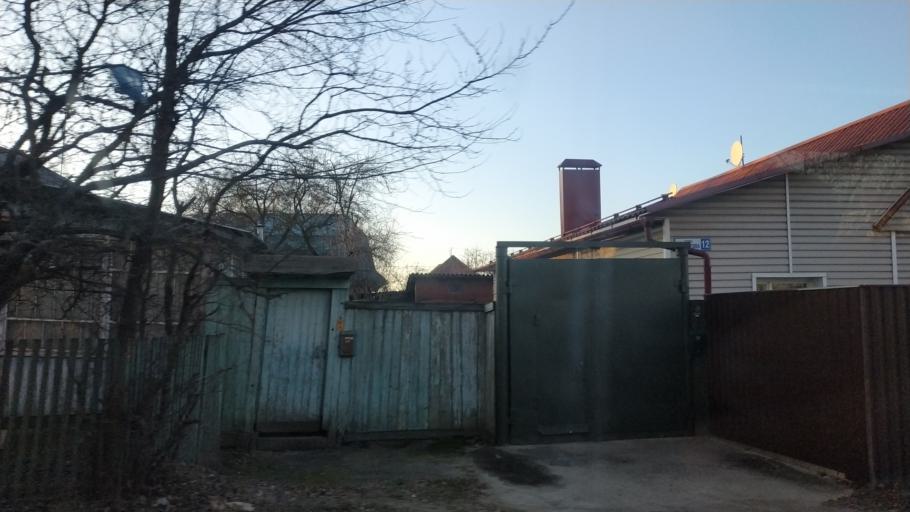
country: RU
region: Moskovskaya
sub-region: Podol'skiy Rayon
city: Podol'sk
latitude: 55.4034
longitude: 37.5552
